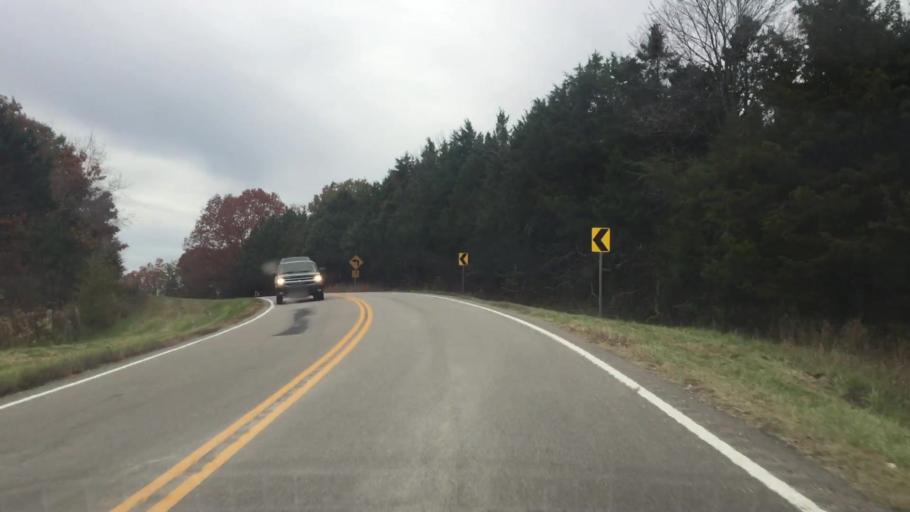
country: US
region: Missouri
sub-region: Gasconade County
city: Hermann
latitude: 38.7245
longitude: -91.7018
